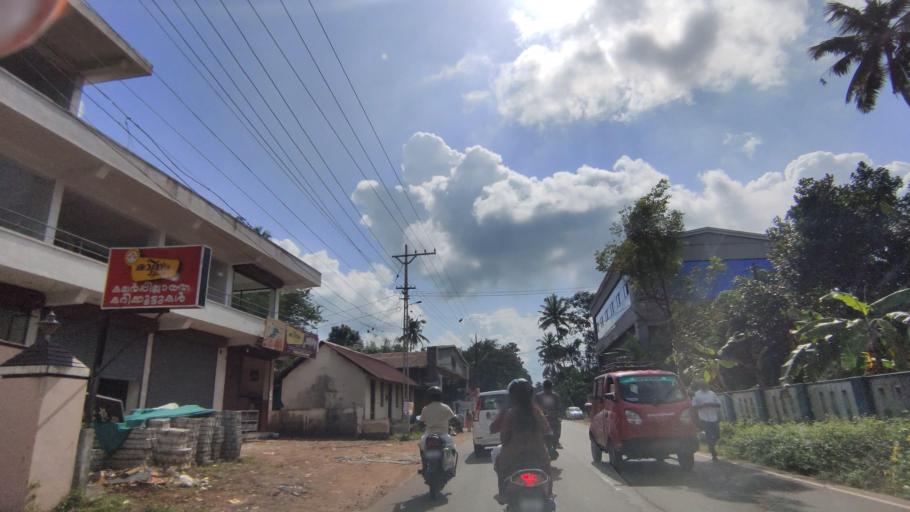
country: IN
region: Kerala
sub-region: Kottayam
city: Kottayam
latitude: 9.6758
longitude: 76.5466
